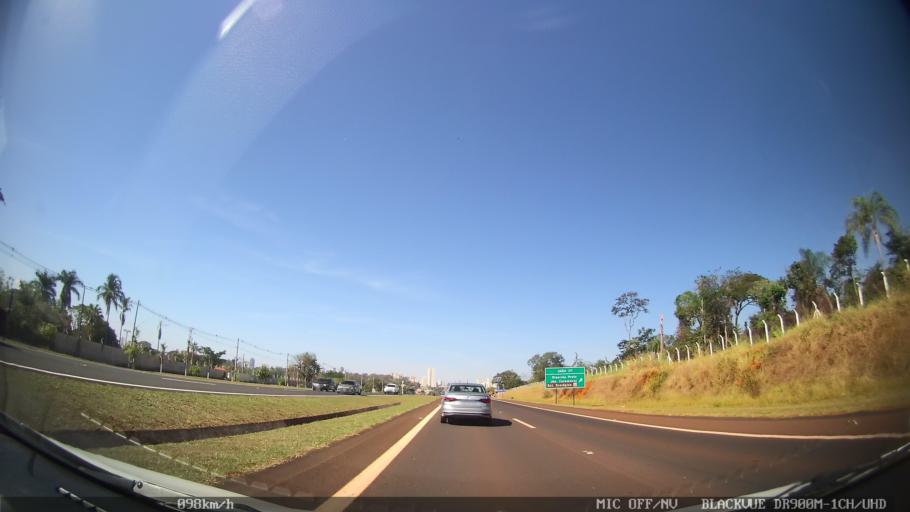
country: BR
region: Sao Paulo
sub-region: Ribeirao Preto
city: Ribeirao Preto
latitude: -21.2130
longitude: -47.8432
